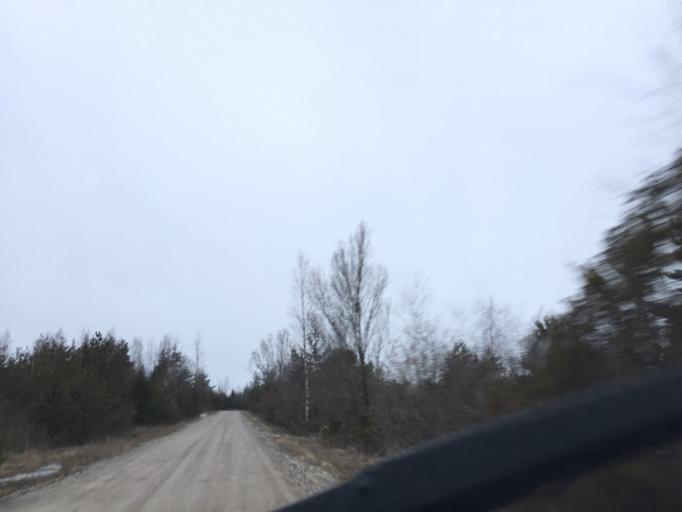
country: EE
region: Laeaene
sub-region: Haapsalu linn
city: Haapsalu
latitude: 58.6832
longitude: 23.5199
